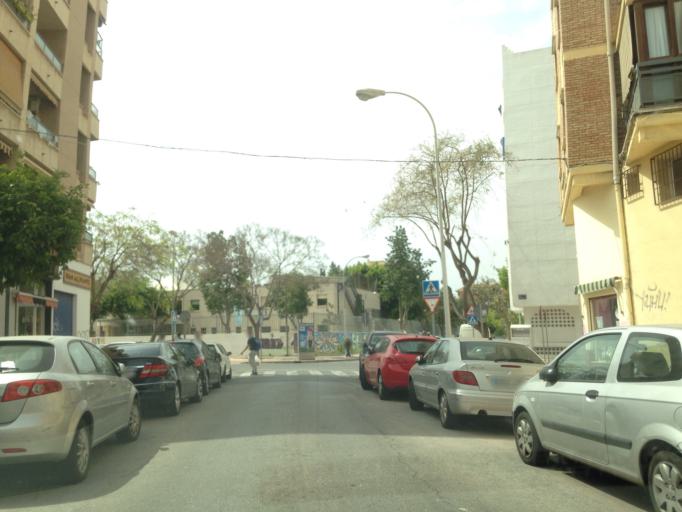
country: ES
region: Andalusia
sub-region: Provincia de Malaga
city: Malaga
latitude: 36.7097
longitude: -4.4301
